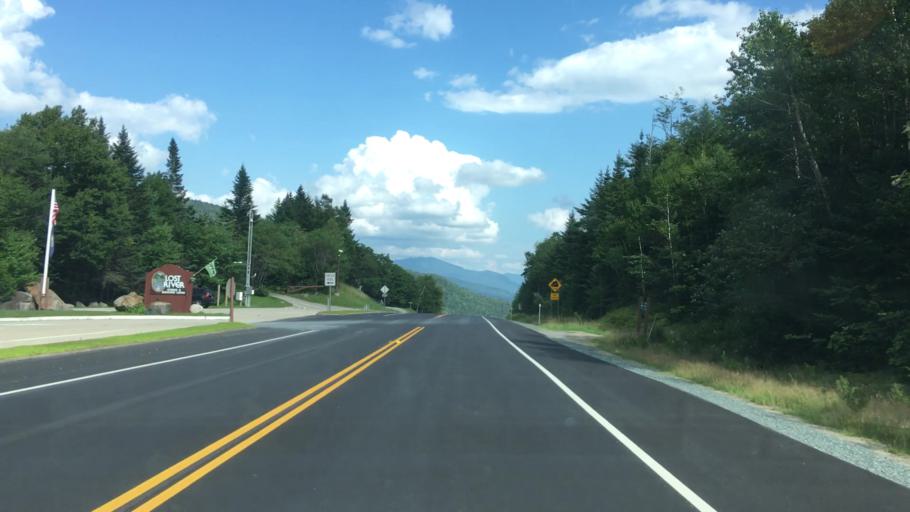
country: US
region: New Hampshire
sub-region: Grafton County
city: Woodstock
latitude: 44.0372
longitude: -71.7856
